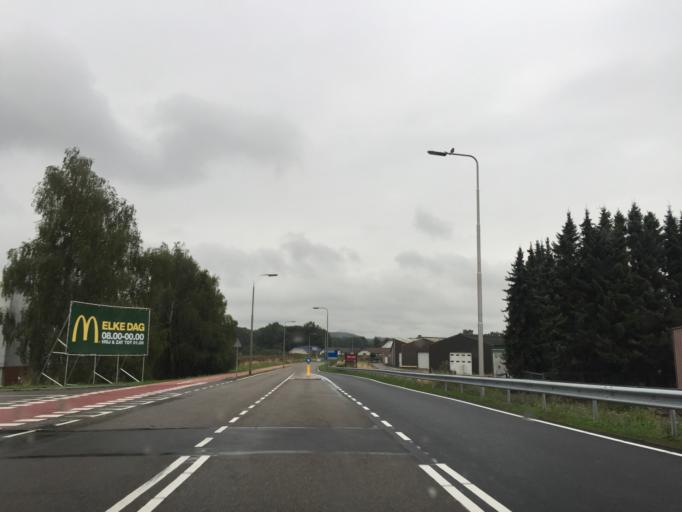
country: NL
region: Limburg
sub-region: Gemeente Maastricht
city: Heer
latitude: 50.8127
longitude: 5.7204
